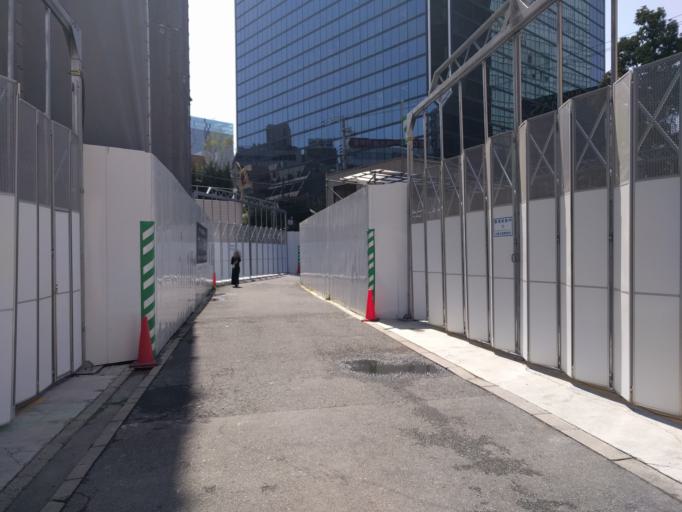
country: JP
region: Osaka
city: Osaka-shi
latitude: 34.7065
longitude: 135.5028
